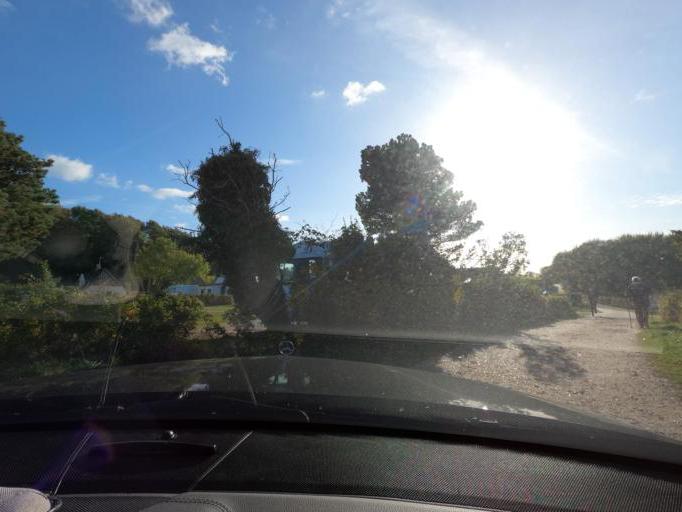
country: DK
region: South Denmark
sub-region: Sonderborg Kommune
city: Dybbol
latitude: 54.8861
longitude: 9.7293
